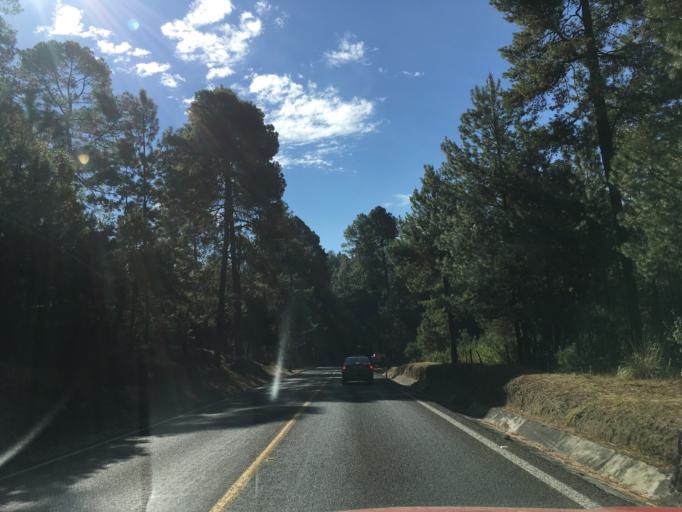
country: MX
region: Michoacan
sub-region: Hidalgo
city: Tierras Coloradas (San Pedro)
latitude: 19.6963
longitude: -100.7416
